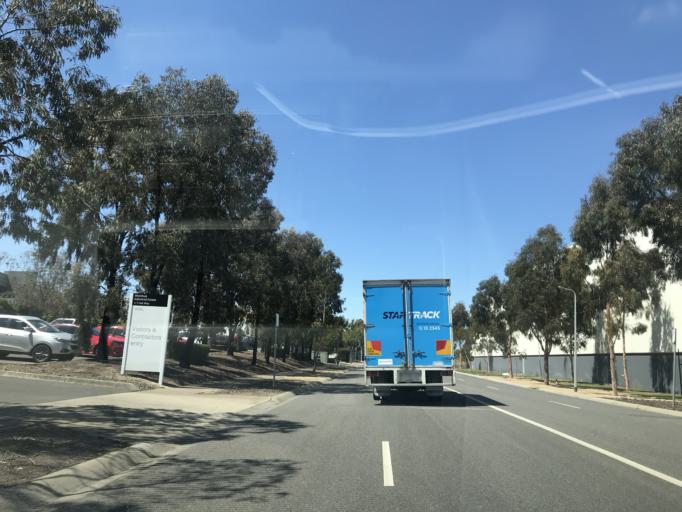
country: AU
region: Victoria
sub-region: Hobsons Bay
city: Laverton
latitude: -37.8398
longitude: 144.7724
